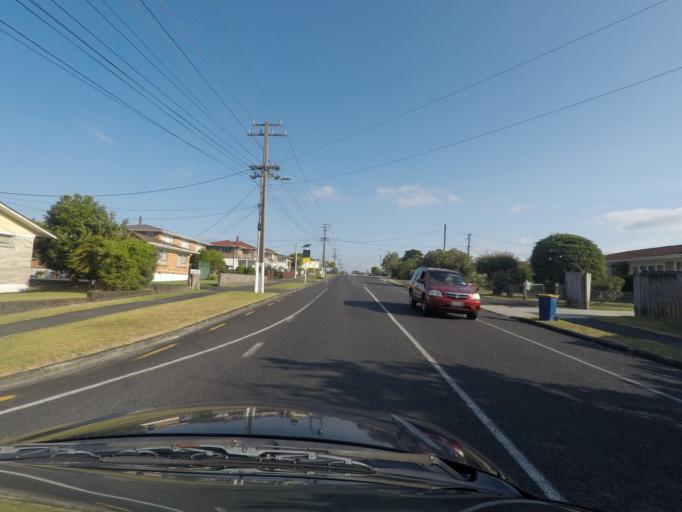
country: NZ
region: Auckland
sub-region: Auckland
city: Rosebank
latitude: -36.8582
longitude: 174.6433
